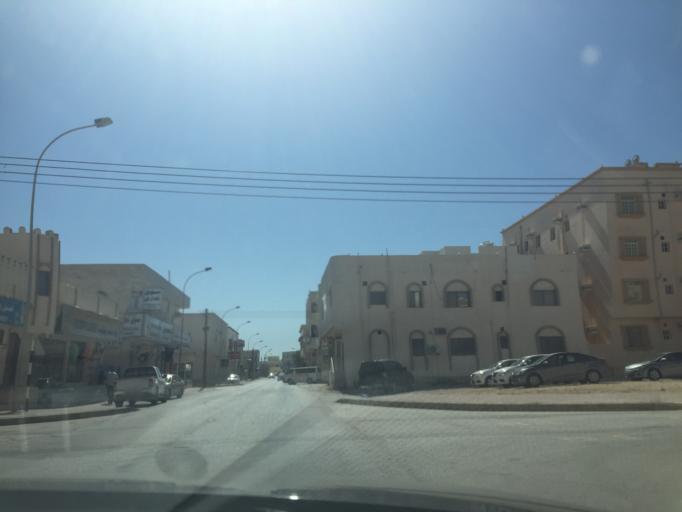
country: OM
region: Zufar
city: Salalah
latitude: 17.0244
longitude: 54.1565
